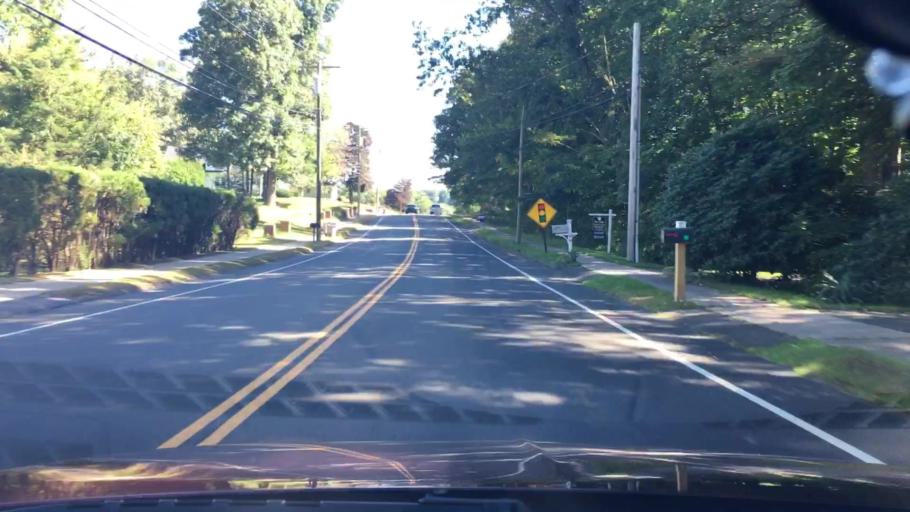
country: US
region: Connecticut
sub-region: Hartford County
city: Bristol
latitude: 41.7035
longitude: -72.9514
